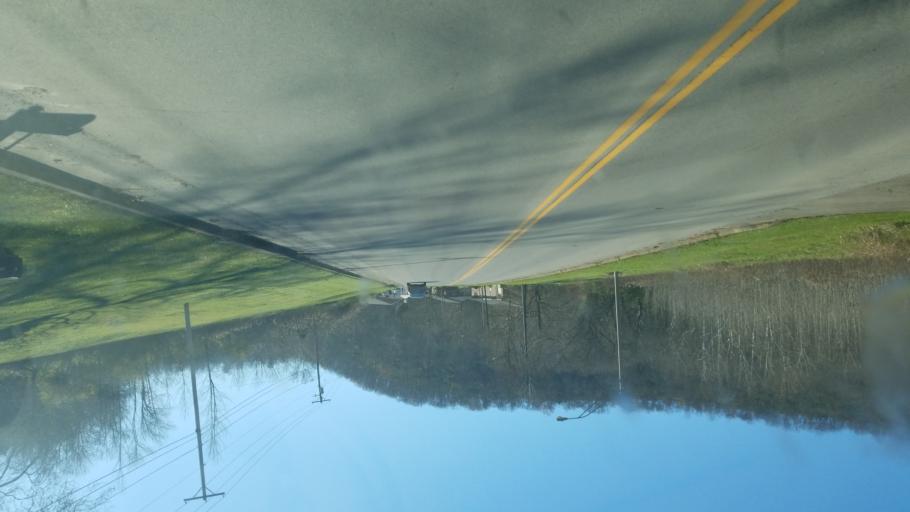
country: US
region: Kentucky
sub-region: Mason County
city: Maysville
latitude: 38.6320
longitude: -83.7514
